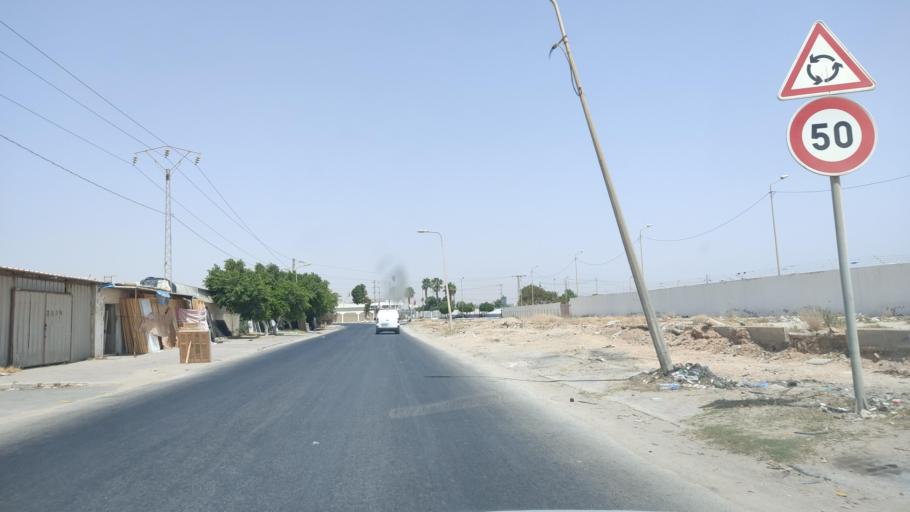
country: TN
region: Safaqis
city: Sfax
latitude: 34.6984
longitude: 10.7197
